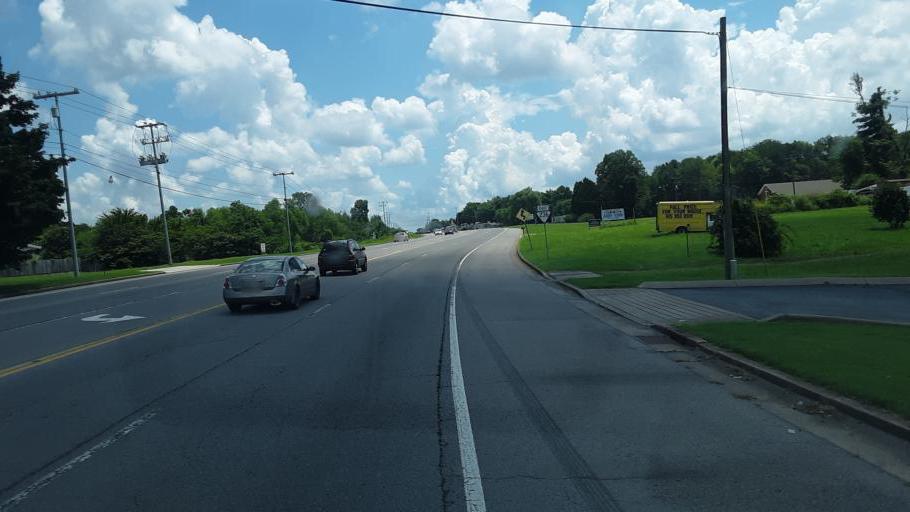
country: US
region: Kentucky
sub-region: Christian County
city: Oak Grove
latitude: 36.6319
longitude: -87.4076
